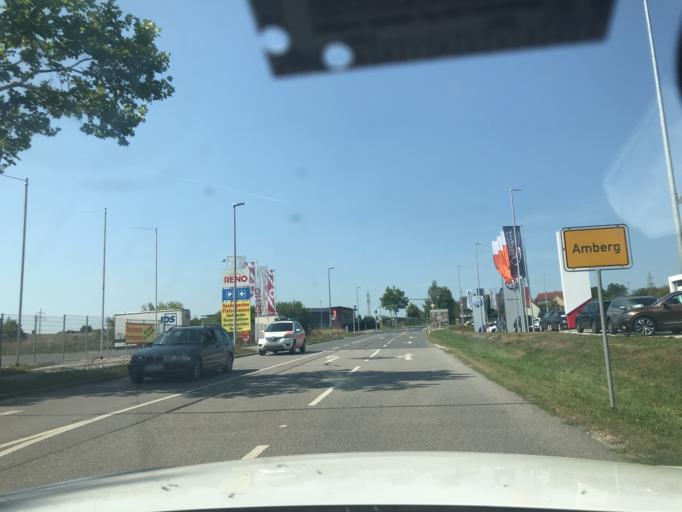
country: DE
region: Bavaria
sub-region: Upper Palatinate
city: Amberg
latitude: 49.4495
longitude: 11.8275
